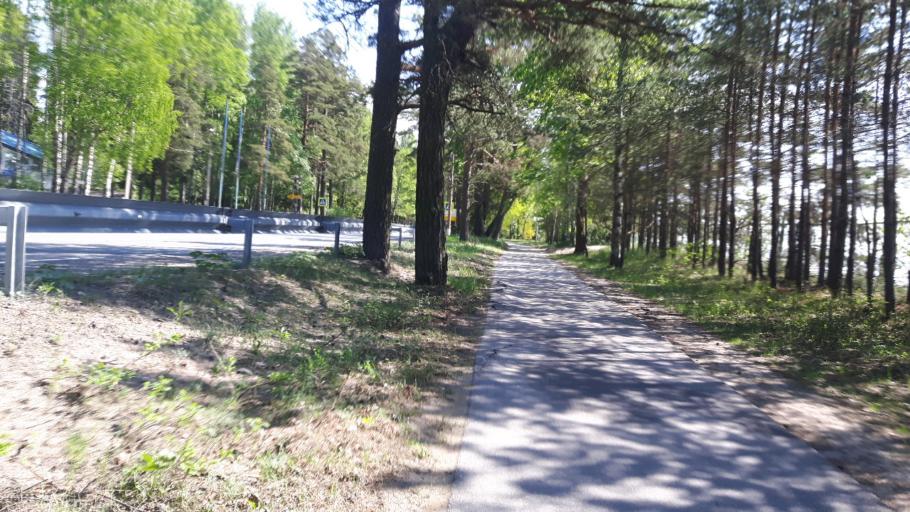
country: RU
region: St.-Petersburg
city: Komarovo
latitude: 60.1729
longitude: 29.8049
